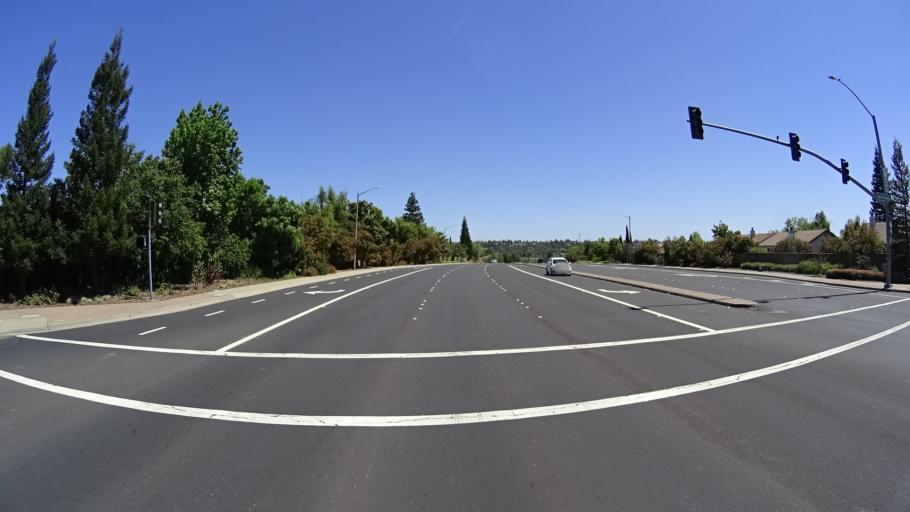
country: US
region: California
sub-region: Placer County
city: Rocklin
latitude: 38.8185
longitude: -121.2734
